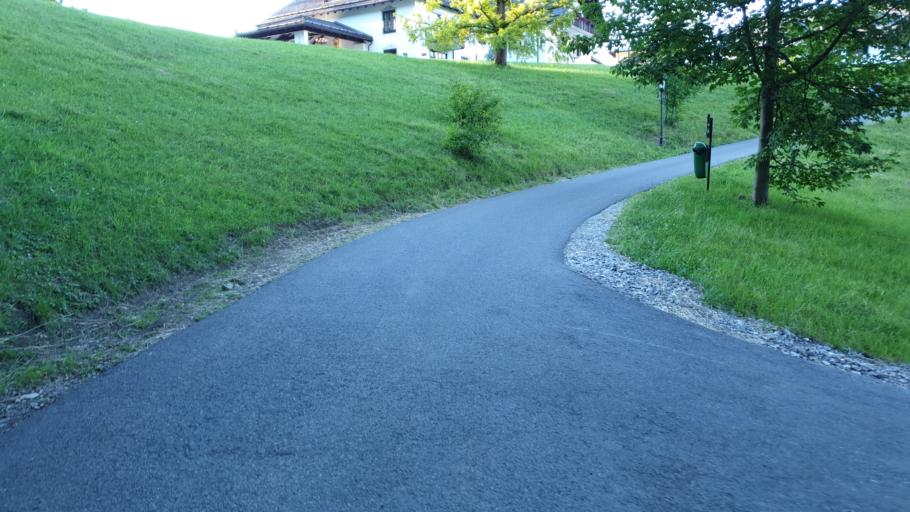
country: AT
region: Salzburg
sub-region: Politischer Bezirk Salzburg-Umgebung
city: Thalgau
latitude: 47.8080
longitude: 13.2549
